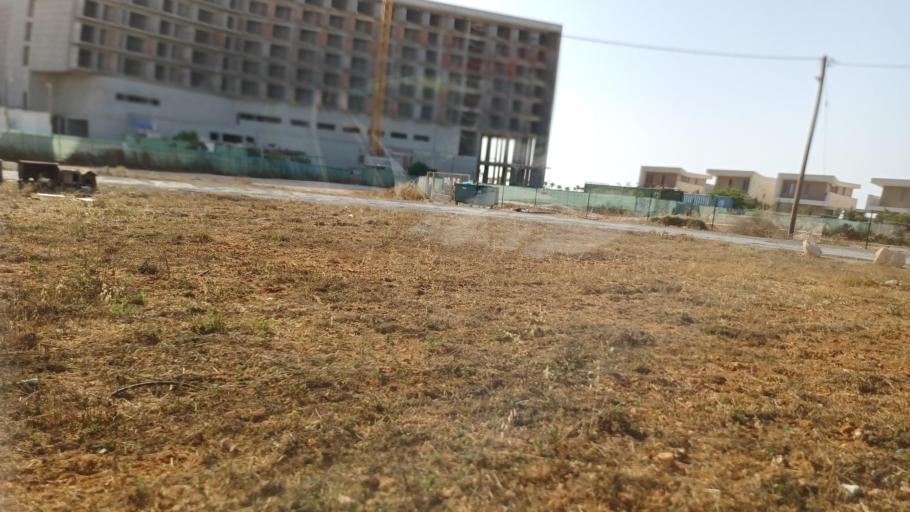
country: CY
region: Ammochostos
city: Liopetri
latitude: 34.9802
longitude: 33.9316
